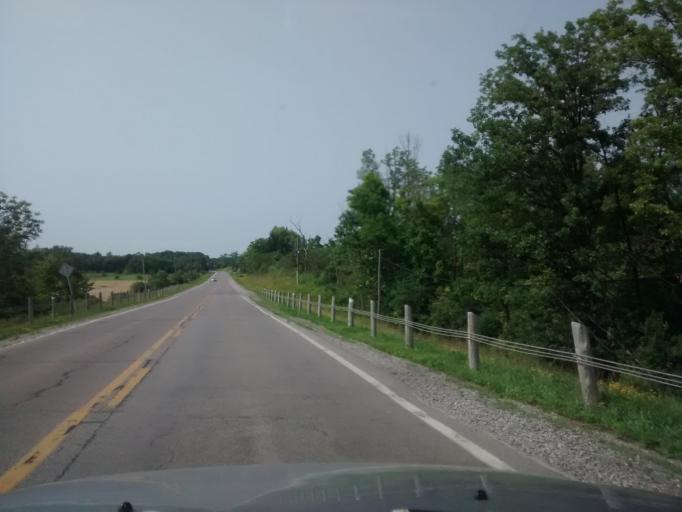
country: CA
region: Ontario
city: Ancaster
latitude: 42.9954
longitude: -79.8659
